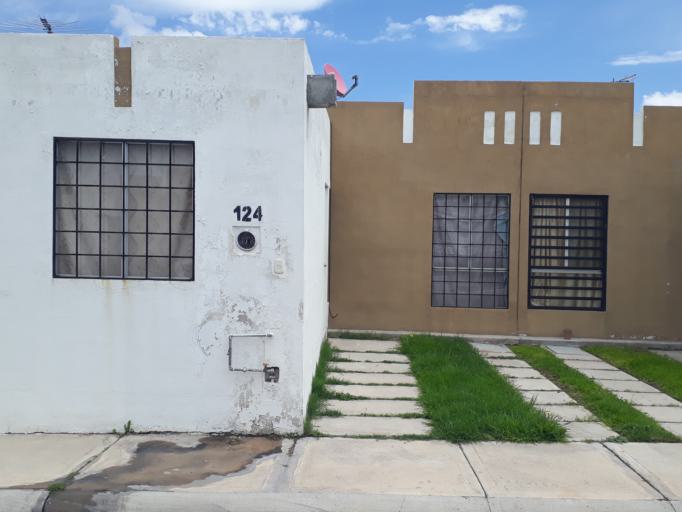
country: MX
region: Aguascalientes
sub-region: Aguascalientes
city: San Sebastian [Fraccionamiento]
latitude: 21.8059
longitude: -102.2685
